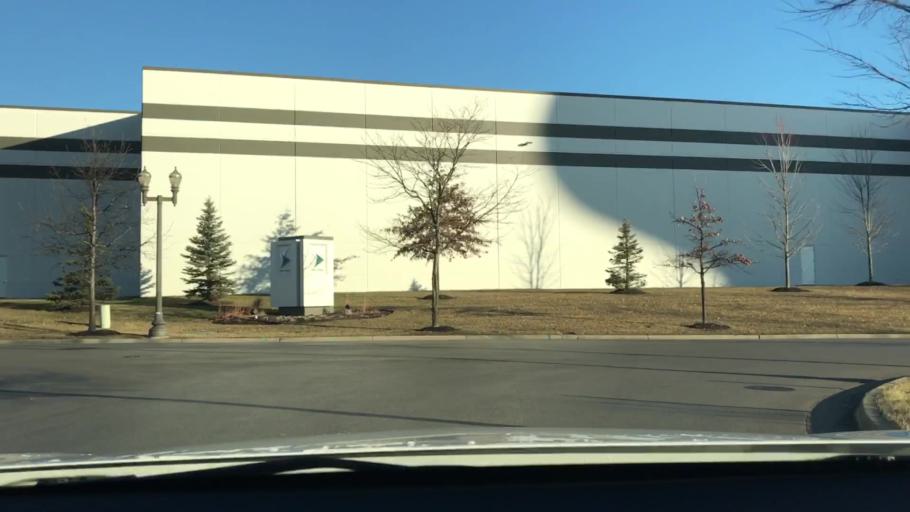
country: US
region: Illinois
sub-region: Kane County
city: Gilberts
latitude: 42.0754
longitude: -88.3466
